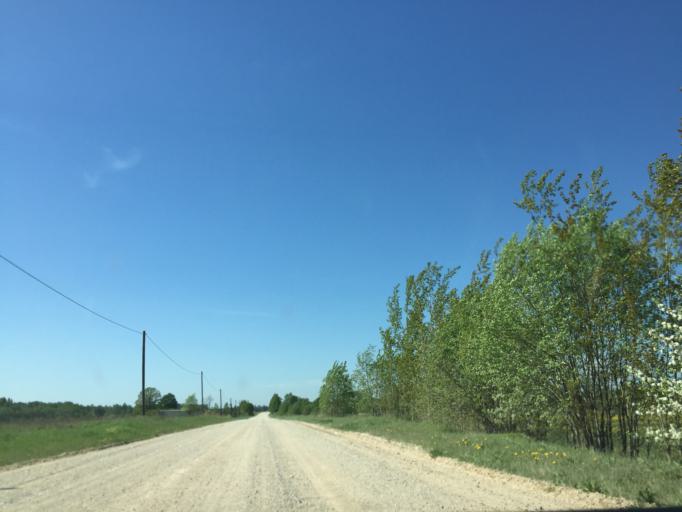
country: LV
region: Kegums
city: Kegums
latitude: 56.8637
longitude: 24.7634
